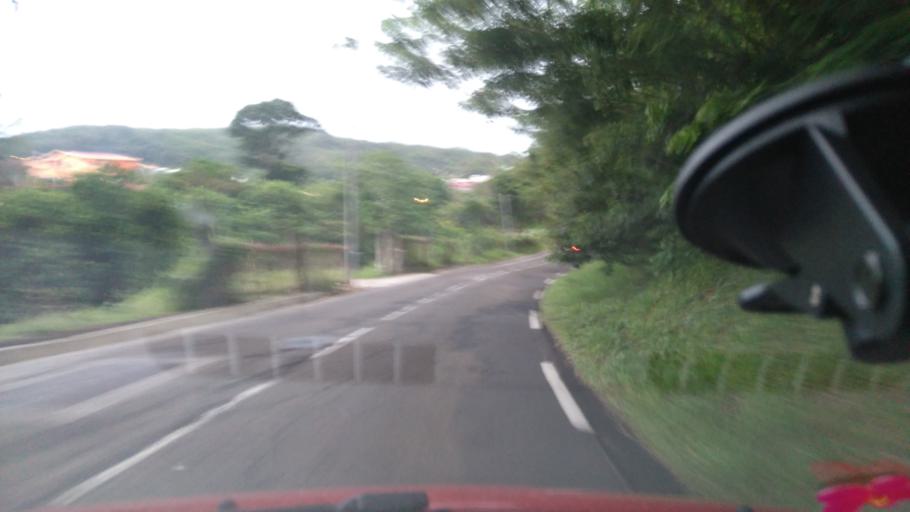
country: MQ
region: Martinique
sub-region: Martinique
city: Saint-Esprit
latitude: 14.5569
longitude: -60.9468
